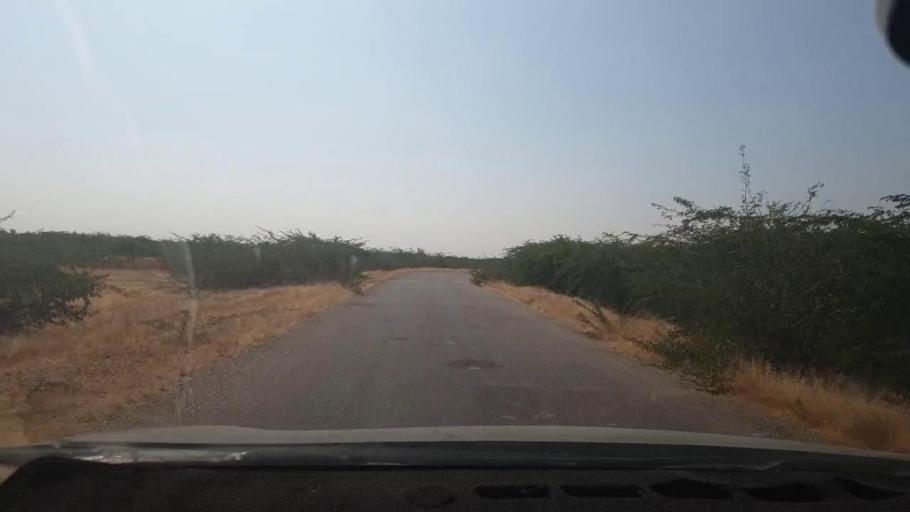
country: PK
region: Sindh
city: Malir Cantonment
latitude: 25.1589
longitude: 67.1503
